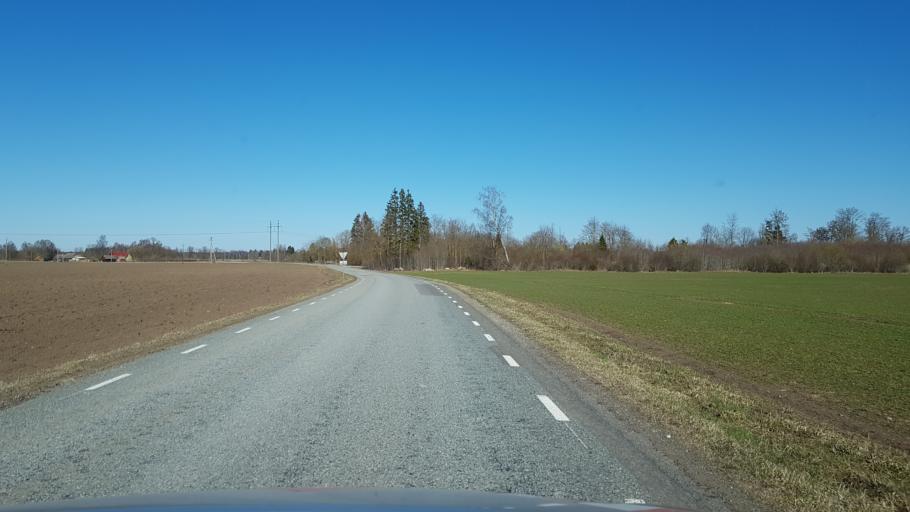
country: EE
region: Laeaene-Virumaa
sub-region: Someru vald
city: Someru
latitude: 59.3713
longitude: 26.4500
